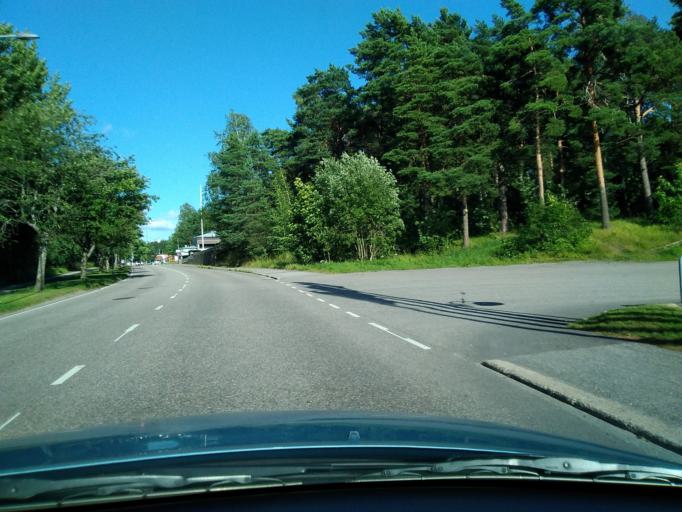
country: FI
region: Uusimaa
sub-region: Raaseporin
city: Ekenaes
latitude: 59.9796
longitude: 23.4496
